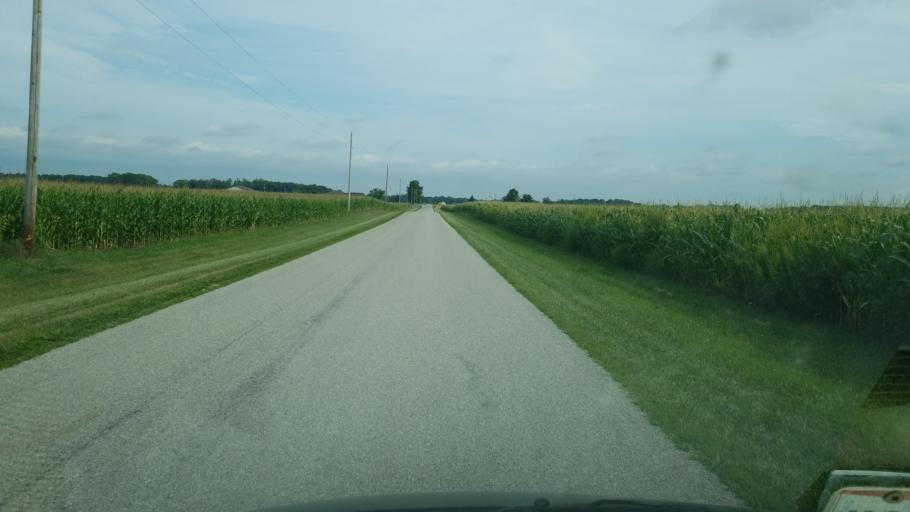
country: US
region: Ohio
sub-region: Seneca County
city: Tiffin
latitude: 41.1351
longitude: -83.0937
